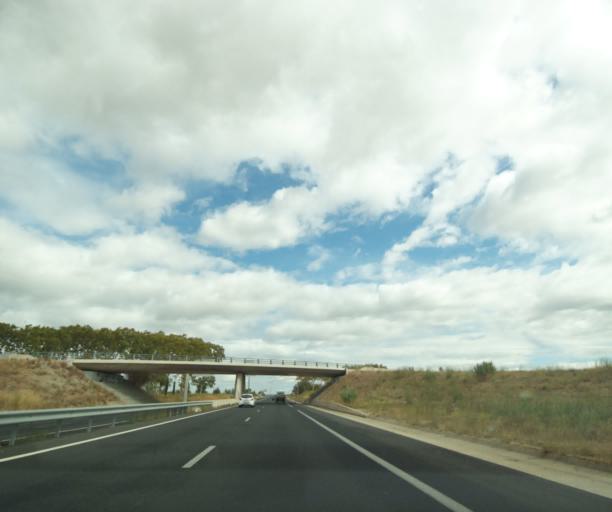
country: FR
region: Languedoc-Roussillon
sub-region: Departement de l'Herault
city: Saint-Andre-de-Sangonis
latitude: 43.6580
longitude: 3.4701
